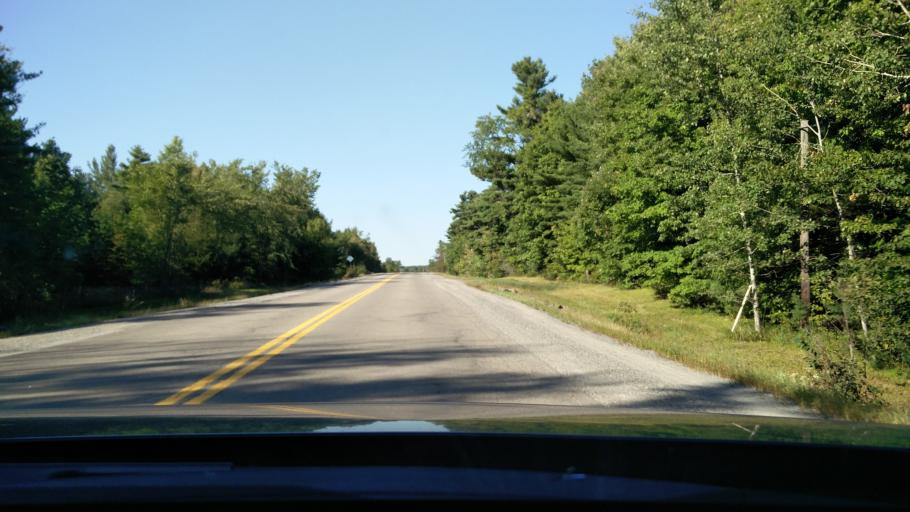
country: CA
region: Ontario
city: Perth
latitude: 44.7186
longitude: -76.4012
